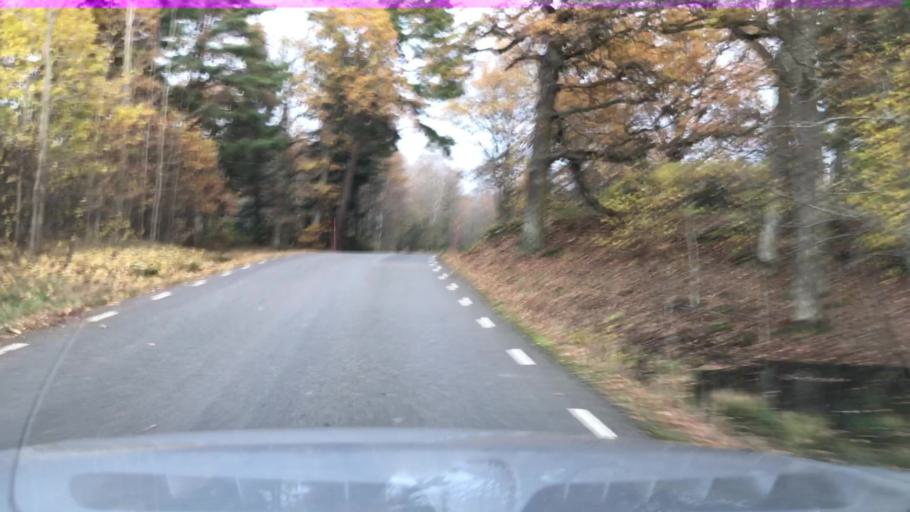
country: SE
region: OEstergoetland
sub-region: Valdemarsviks Kommun
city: Valdemarsvik
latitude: 58.2859
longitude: 16.7617
